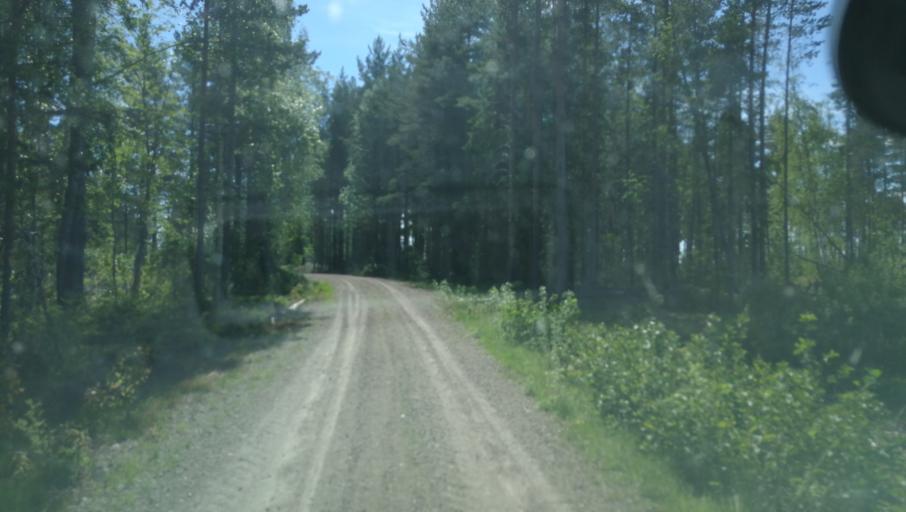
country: SE
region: Dalarna
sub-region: Vansbro Kommun
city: Vansbro
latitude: 60.8271
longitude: 14.1816
